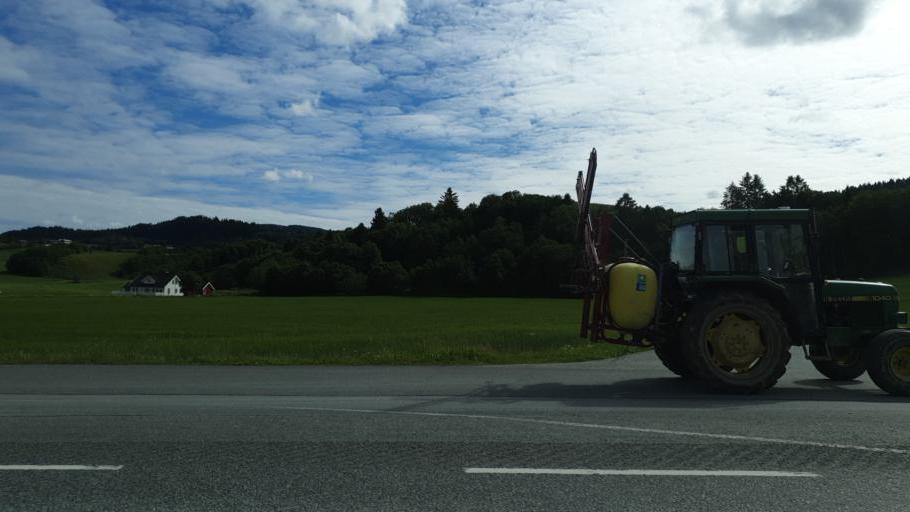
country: NO
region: Sor-Trondelag
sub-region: Melhus
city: Lundamo
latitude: 63.1772
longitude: 10.3168
